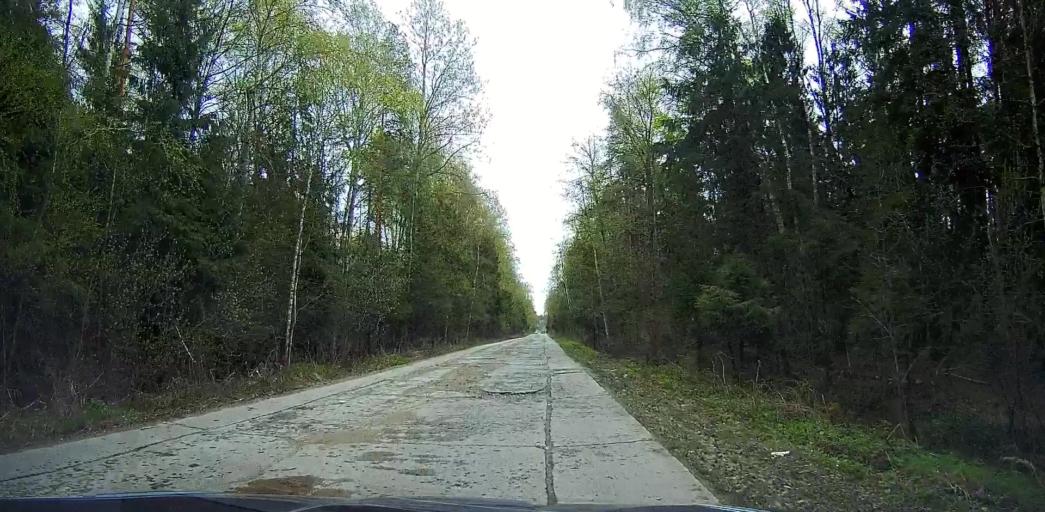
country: RU
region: Moskovskaya
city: Malyshevo
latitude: 55.5347
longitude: 38.3916
